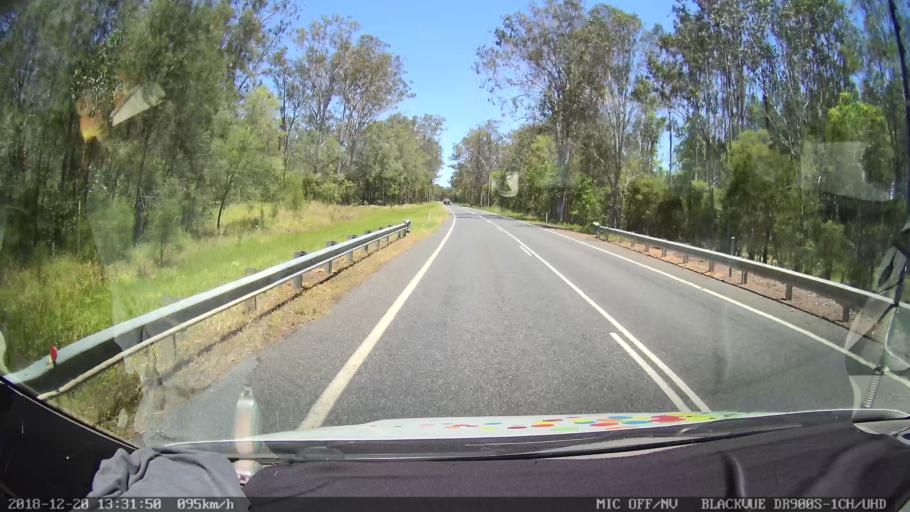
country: AU
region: New South Wales
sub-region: Clarence Valley
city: Gordon
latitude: -29.2236
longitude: 152.9876
